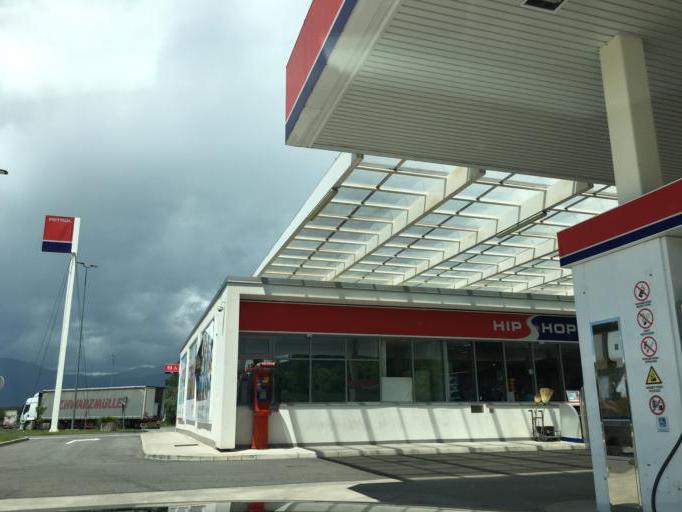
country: SI
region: Vipava
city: Vipava
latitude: 45.8291
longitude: 13.9588
